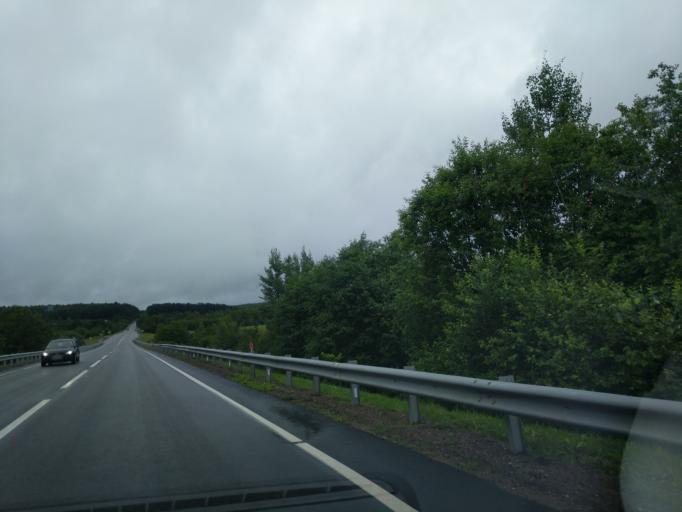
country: BY
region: Minsk
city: Syomkava
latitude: 54.1812
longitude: 27.5005
